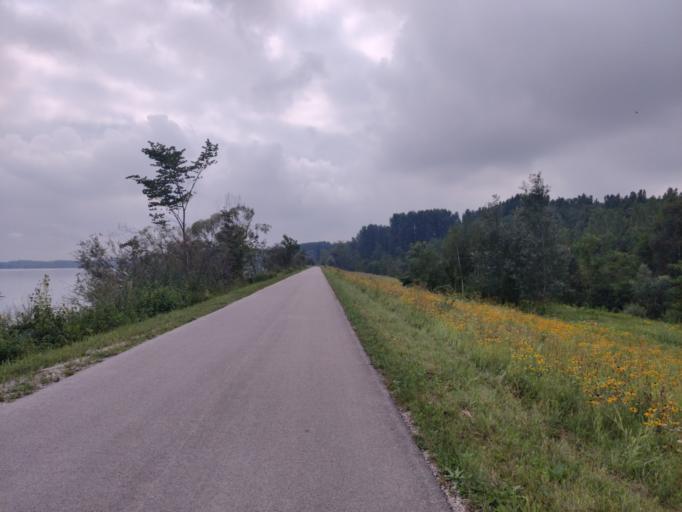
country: AT
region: Lower Austria
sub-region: Politischer Bezirk Sankt Polten
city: Traismauer
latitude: 48.3748
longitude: 15.7338
